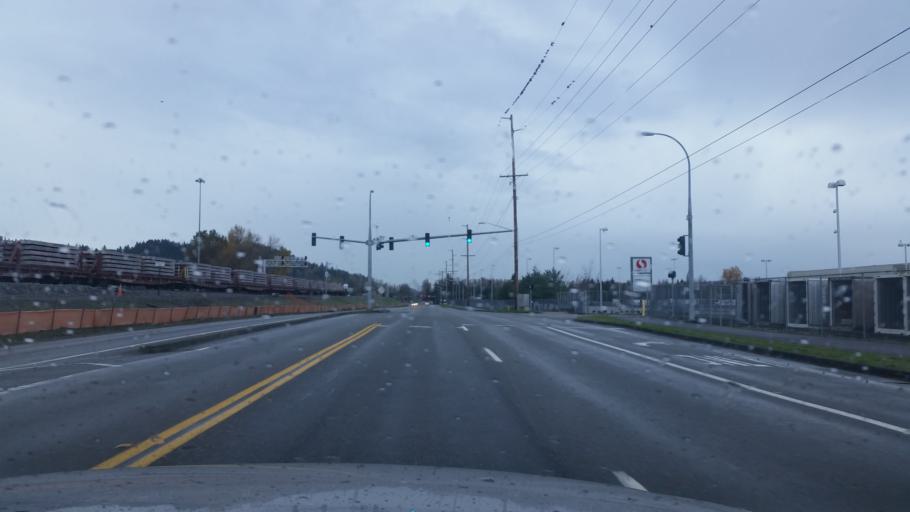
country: US
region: Washington
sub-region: King County
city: Algona
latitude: 47.2768
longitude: -122.2311
